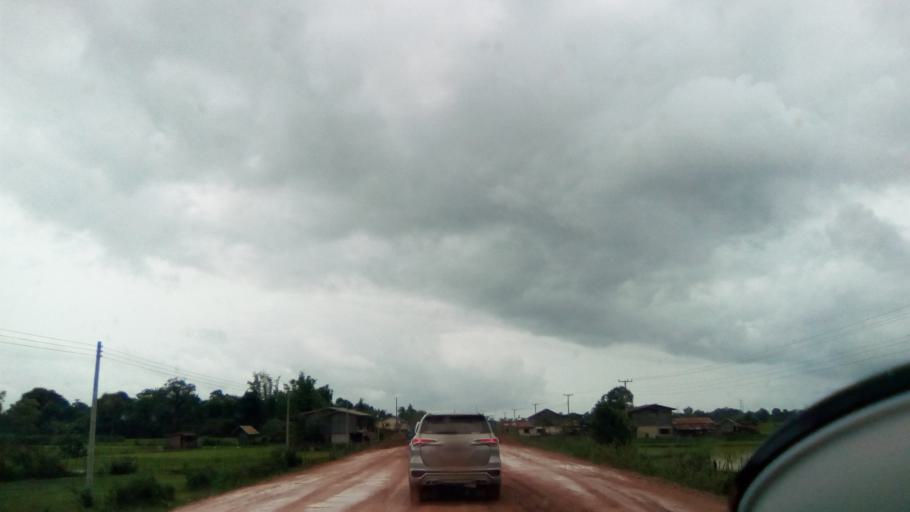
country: LA
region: Attapu
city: Attapu
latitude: 14.7364
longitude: 106.6872
